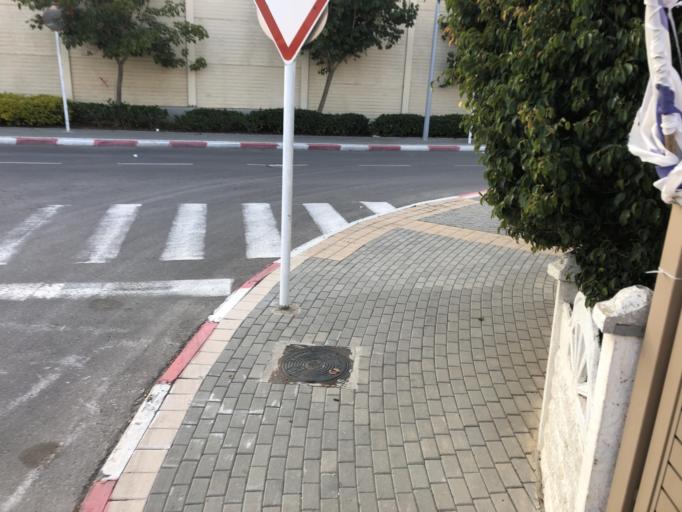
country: IL
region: Northern District
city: `Akko
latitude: 32.9254
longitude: 35.0846
